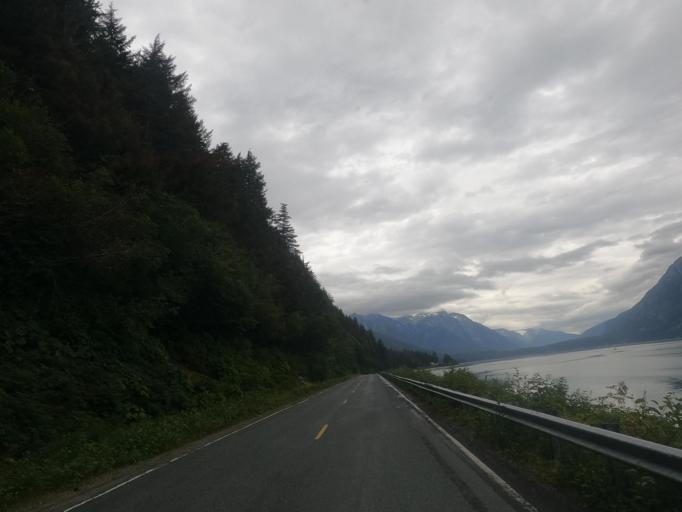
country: US
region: Alaska
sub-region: Haines Borough
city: Haines
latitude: 59.2917
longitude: -135.4976
